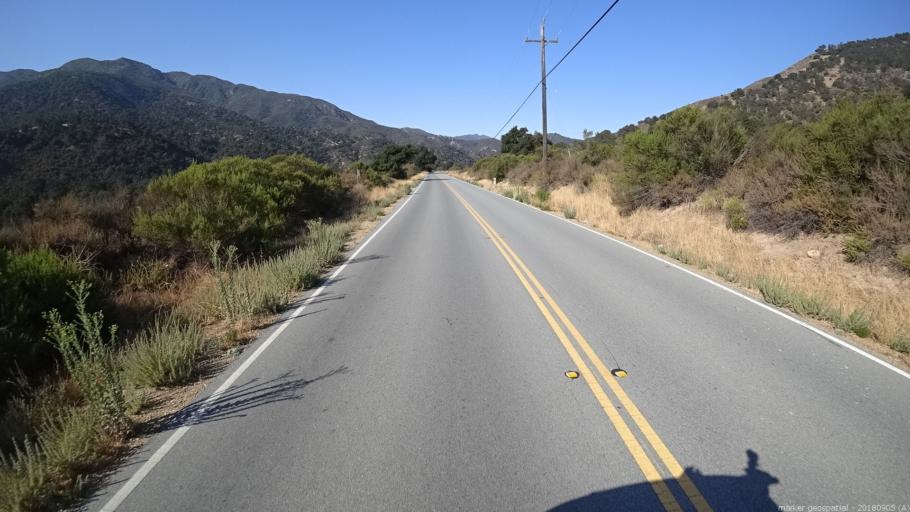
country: US
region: California
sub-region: Monterey County
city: Greenfield
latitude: 36.2343
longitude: -121.4544
